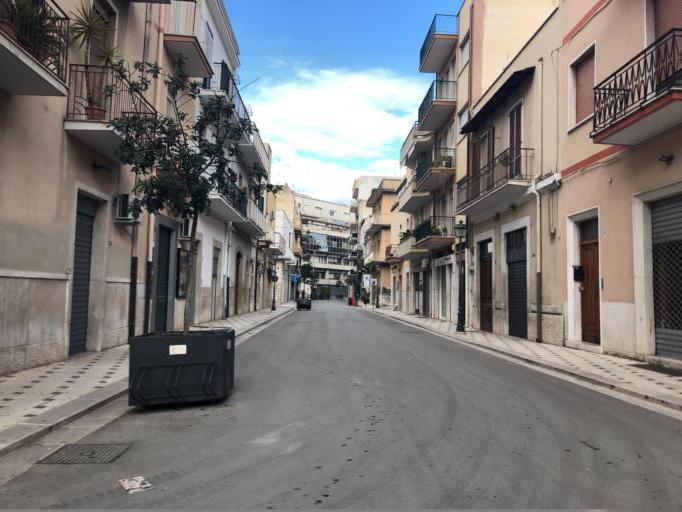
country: IT
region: Apulia
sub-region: Provincia di Barletta - Andria - Trani
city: Andria
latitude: 41.2281
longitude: 16.3022
